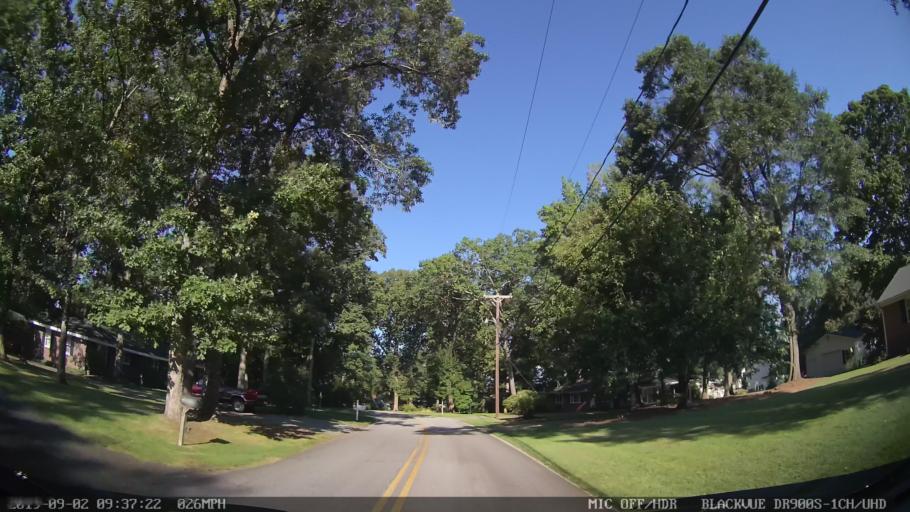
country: US
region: South Carolina
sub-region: Spartanburg County
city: Fairforest
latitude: 34.9394
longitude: -82.0078
